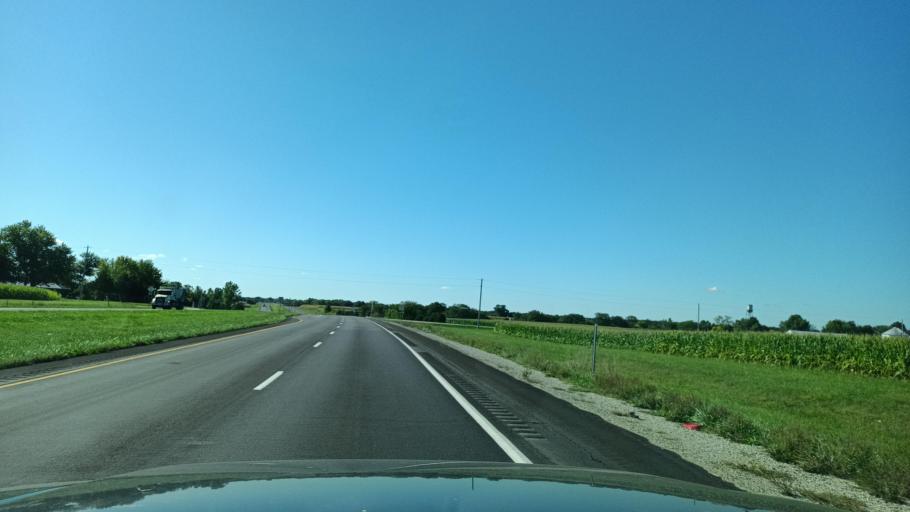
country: US
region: Iowa
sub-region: Lee County
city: Keokuk
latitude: 40.4670
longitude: -91.4449
